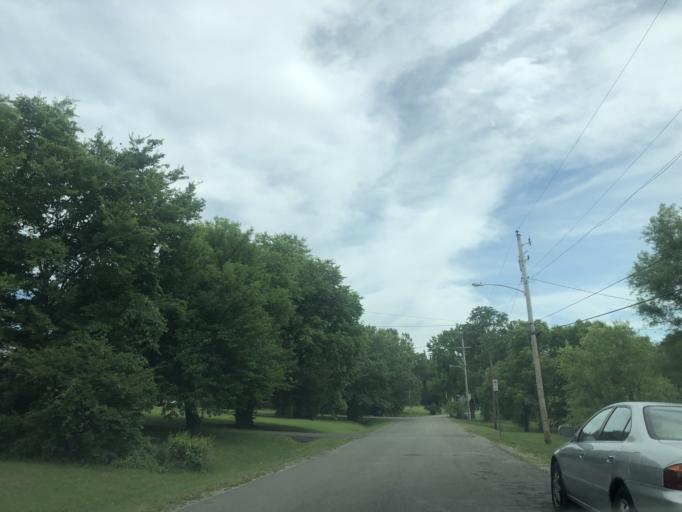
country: US
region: Tennessee
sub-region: Davidson County
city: Nashville
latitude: 36.2160
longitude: -86.8063
